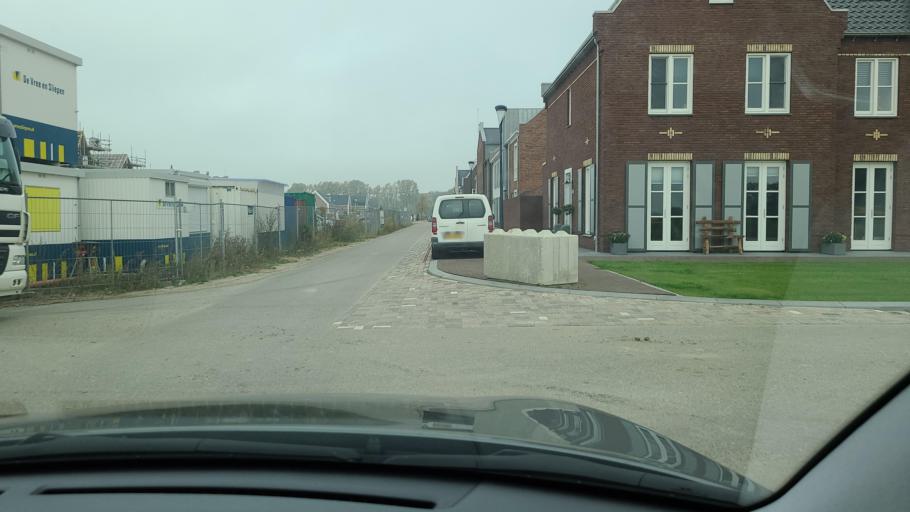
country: NL
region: Gelderland
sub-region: Gemeente Geldermalsen
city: Geldermalsen
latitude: 51.8678
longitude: 5.2933
